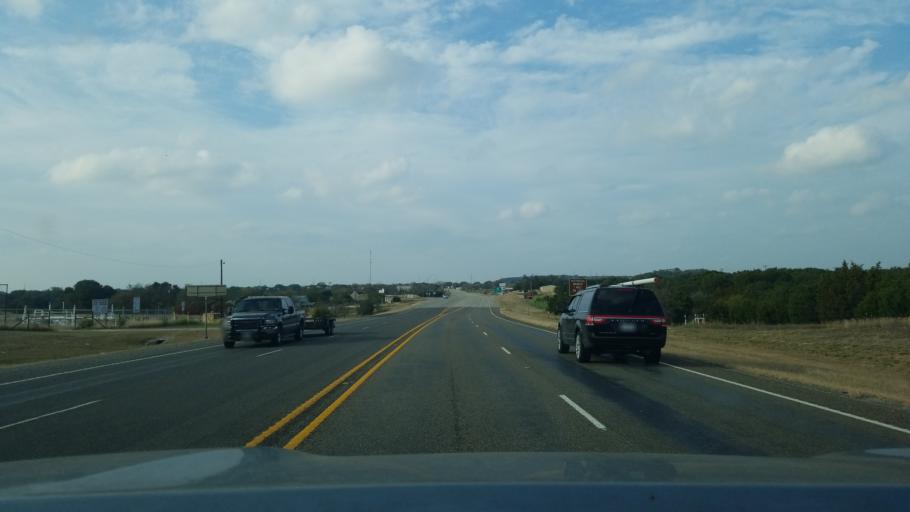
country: US
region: Texas
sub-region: Lampasas County
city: Lampasas
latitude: 31.2028
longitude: -98.3870
